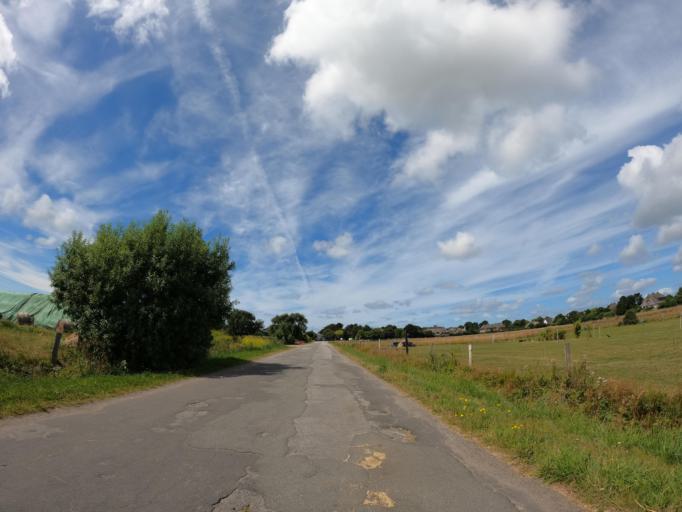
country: DE
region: Schleswig-Holstein
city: Keitum
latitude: 54.8877
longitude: 8.3771
